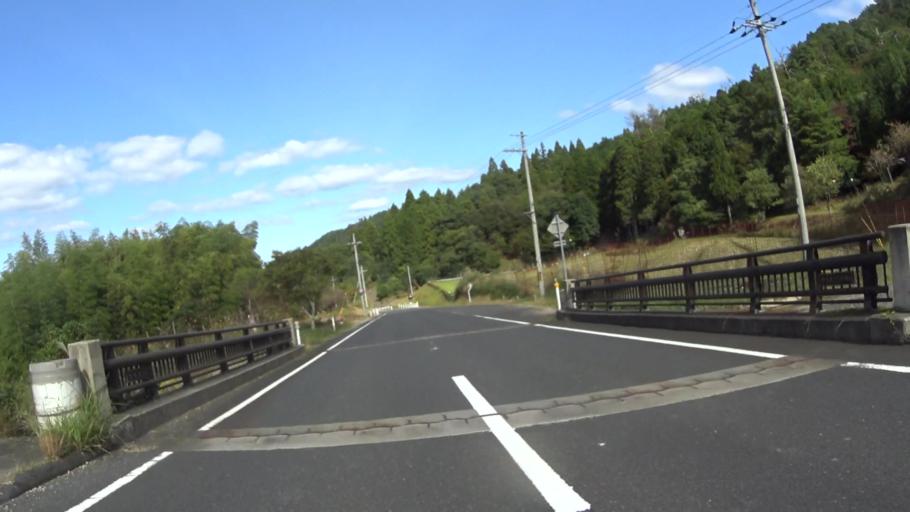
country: JP
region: Hyogo
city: Toyooka
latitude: 35.5410
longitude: 134.9772
